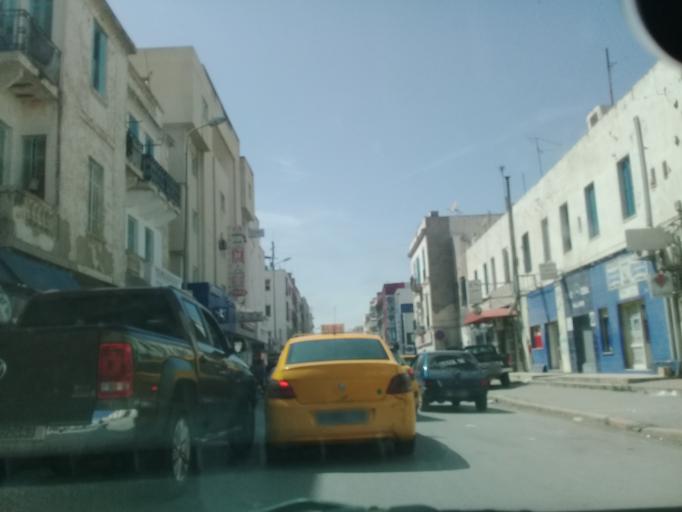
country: TN
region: Tunis
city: Tunis
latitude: 36.8114
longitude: 10.1766
